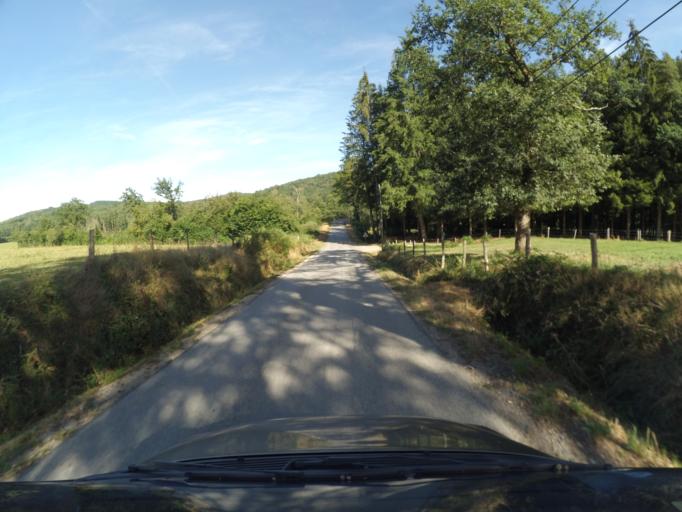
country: FR
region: Limousin
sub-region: Departement de la Correze
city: Bugeat
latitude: 45.7068
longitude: 1.8673
